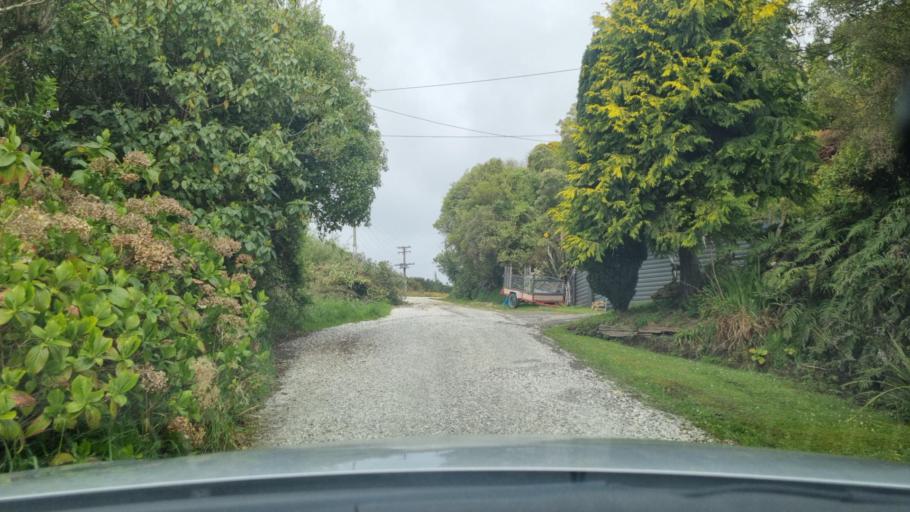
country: NZ
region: Southland
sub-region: Invercargill City
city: Bluff
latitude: -46.5762
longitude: 168.2982
